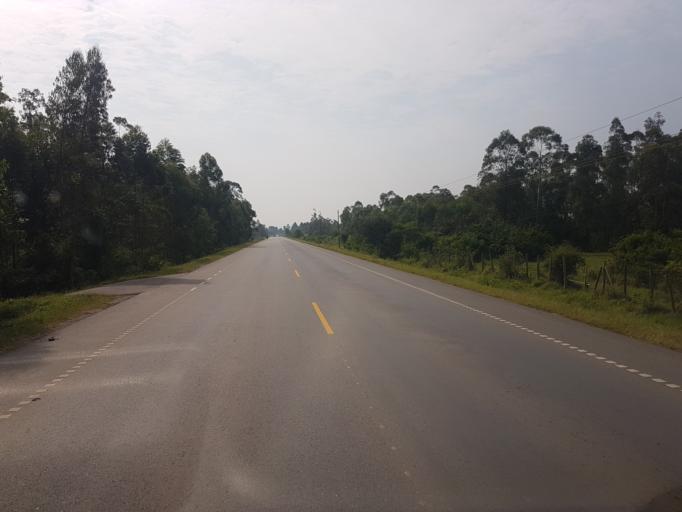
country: UG
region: Western Region
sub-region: Sheema District
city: Kibingo
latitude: -0.6350
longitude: 30.5277
